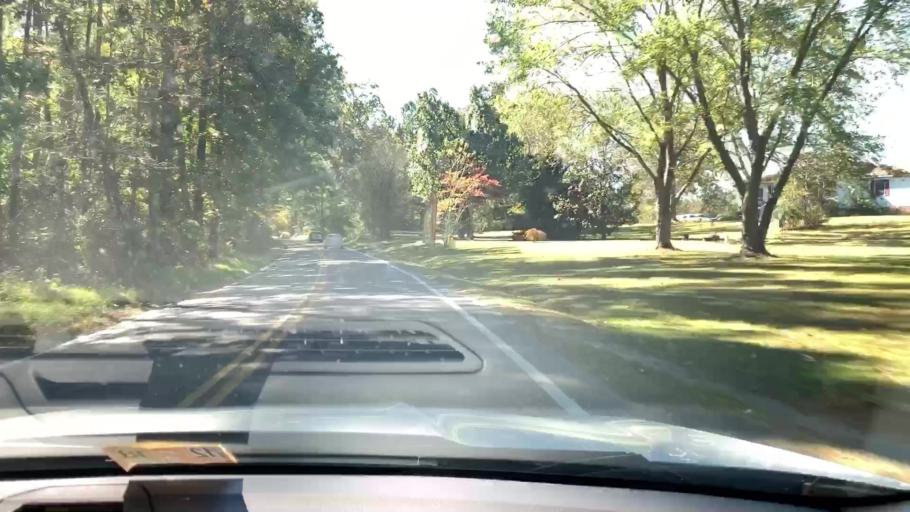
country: US
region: Virginia
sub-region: King William County
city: West Point
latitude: 37.4671
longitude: -76.8358
